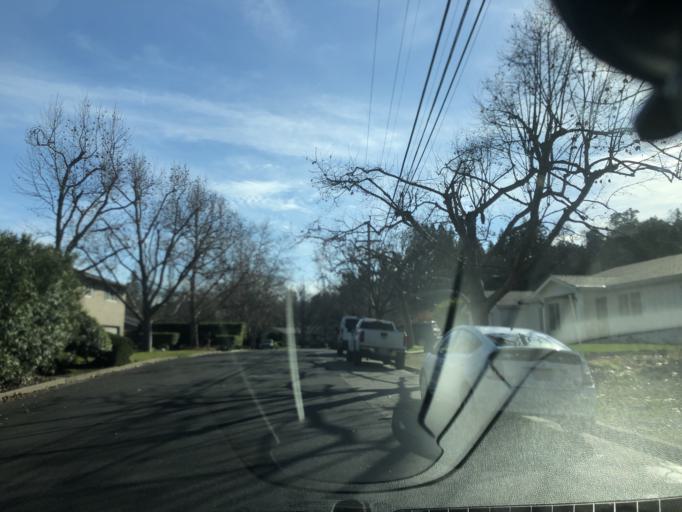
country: US
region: California
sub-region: Contra Costa County
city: Saranap
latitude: 37.8856
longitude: -122.0618
